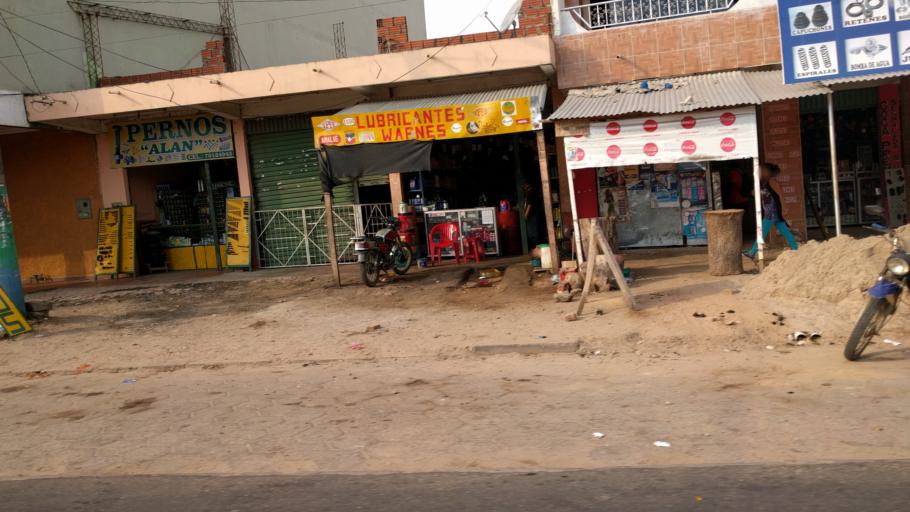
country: BO
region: Santa Cruz
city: Warnes
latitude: -17.5167
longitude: -63.1647
